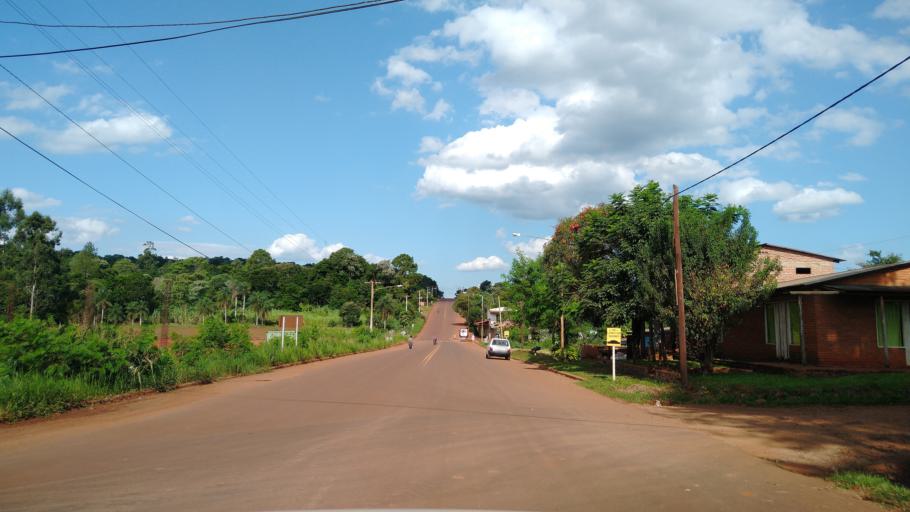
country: AR
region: Misiones
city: Puerto Piray
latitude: -26.4671
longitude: -54.7023
